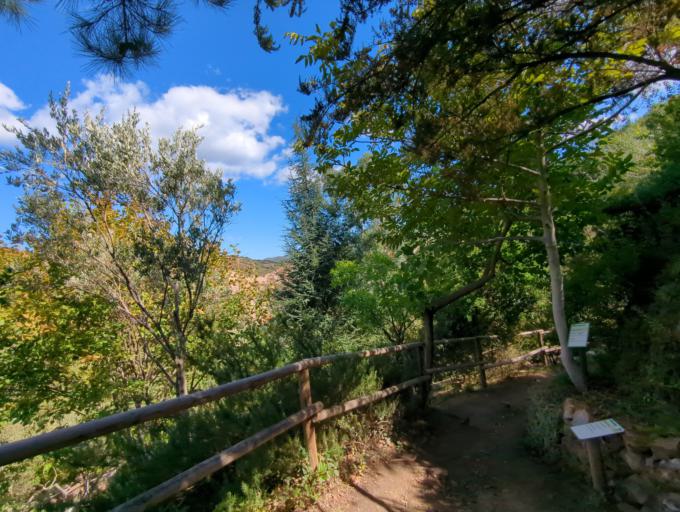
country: GR
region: Crete
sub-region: Nomos Chanias
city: Galatas
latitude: 35.4186
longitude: 23.9382
